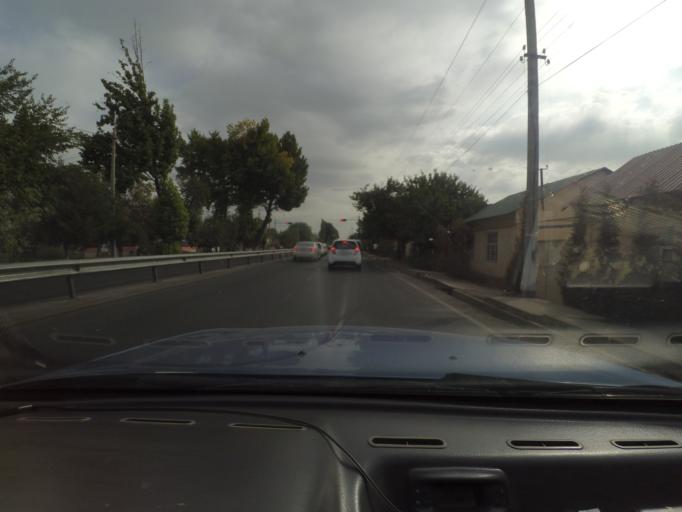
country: UZ
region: Toshkent
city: Qibray
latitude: 41.3997
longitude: 69.4892
